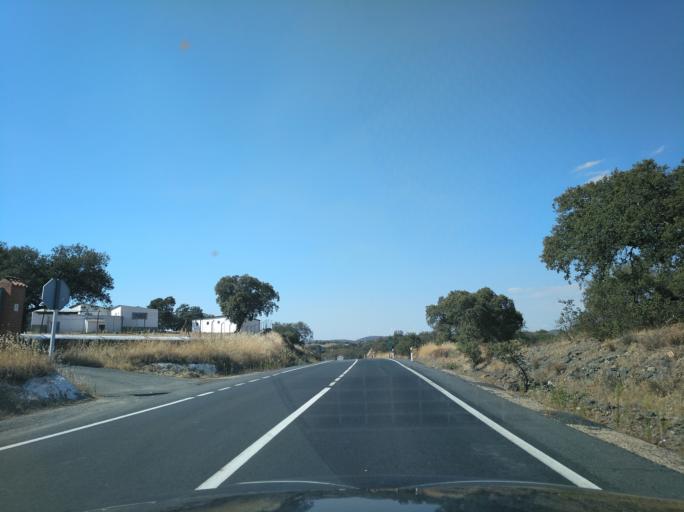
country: ES
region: Andalusia
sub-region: Provincia de Huelva
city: Alosno
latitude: 37.5197
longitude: -7.1342
